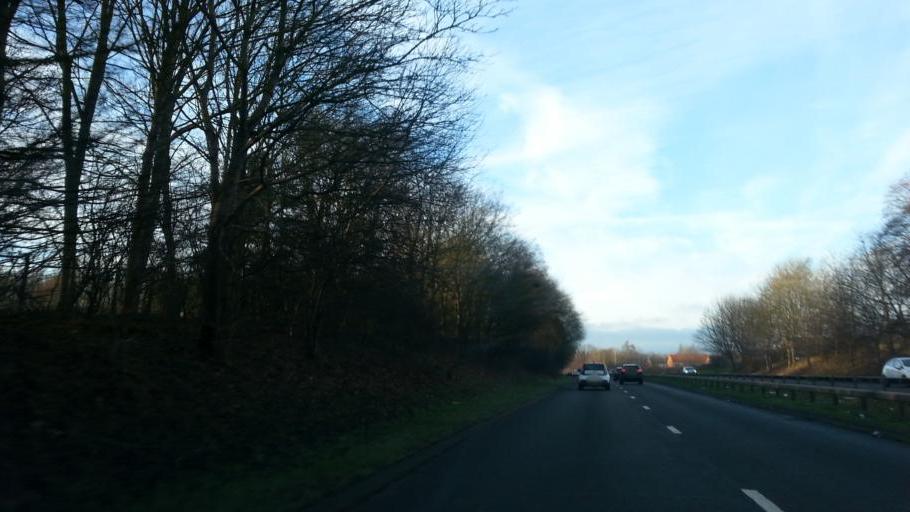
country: GB
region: England
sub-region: Northamptonshire
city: Hardingstone
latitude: 52.2198
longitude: -0.9171
